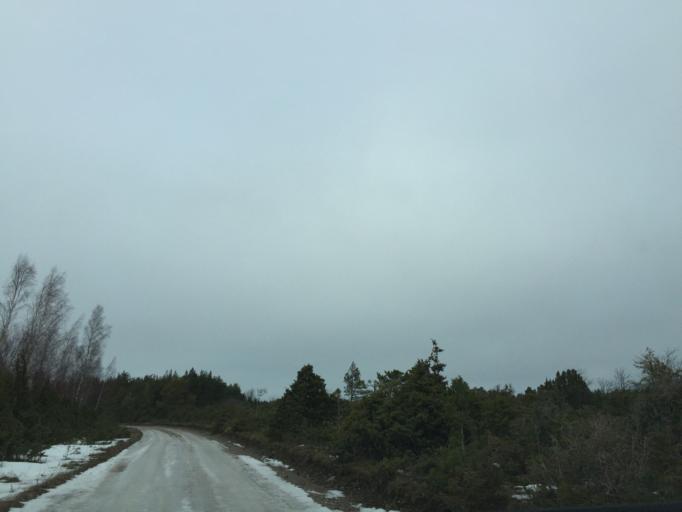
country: EE
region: Saare
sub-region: Kuressaare linn
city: Kuressaare
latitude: 58.4989
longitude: 21.9240
